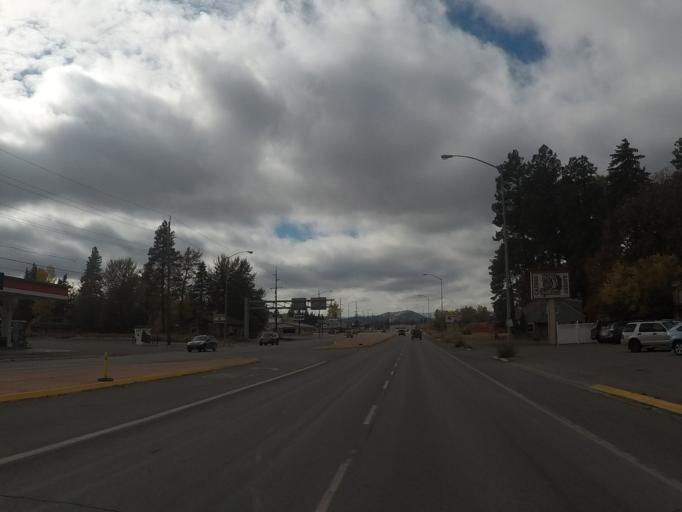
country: US
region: Montana
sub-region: Flathead County
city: Evergreen
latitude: 48.2129
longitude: -114.2811
